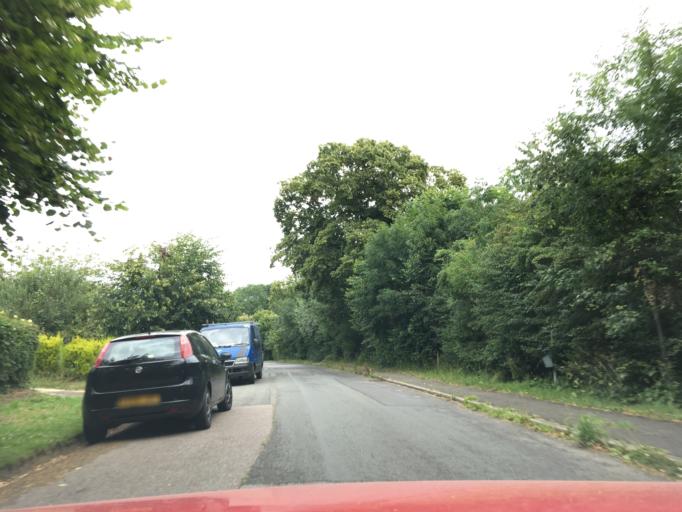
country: GB
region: England
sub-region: Oxfordshire
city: Charlbury
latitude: 51.9193
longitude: -1.4545
